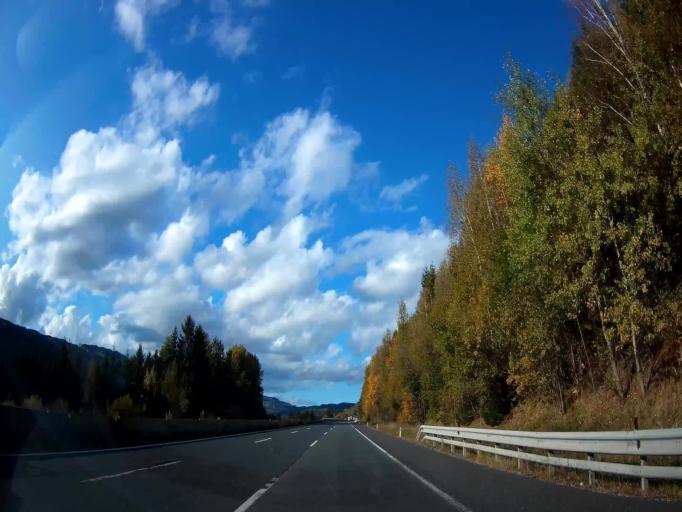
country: AT
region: Carinthia
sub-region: Politischer Bezirk Wolfsberg
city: Wolfsberg
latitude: 46.8711
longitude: 14.8350
